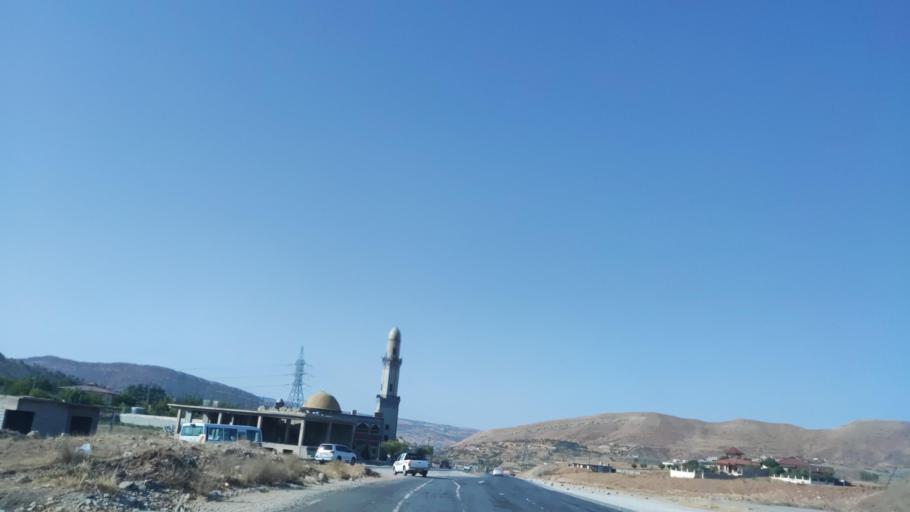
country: IQ
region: Arbil
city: Shaqlawah
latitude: 36.4281
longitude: 44.2697
